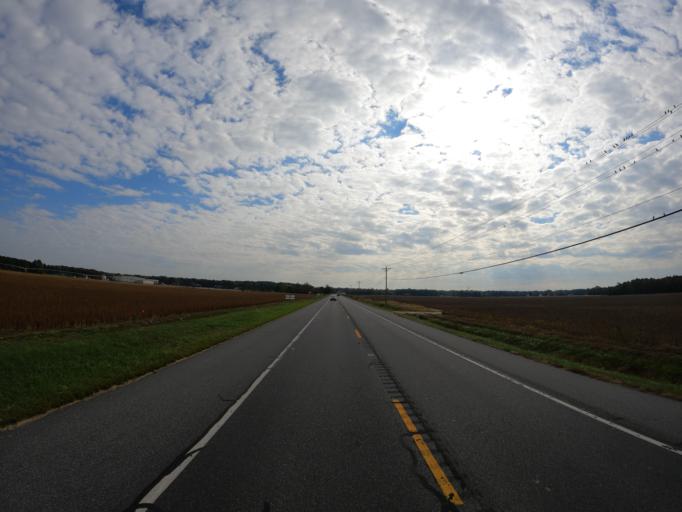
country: US
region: Delaware
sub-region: Sussex County
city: Georgetown
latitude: 38.6964
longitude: -75.4909
